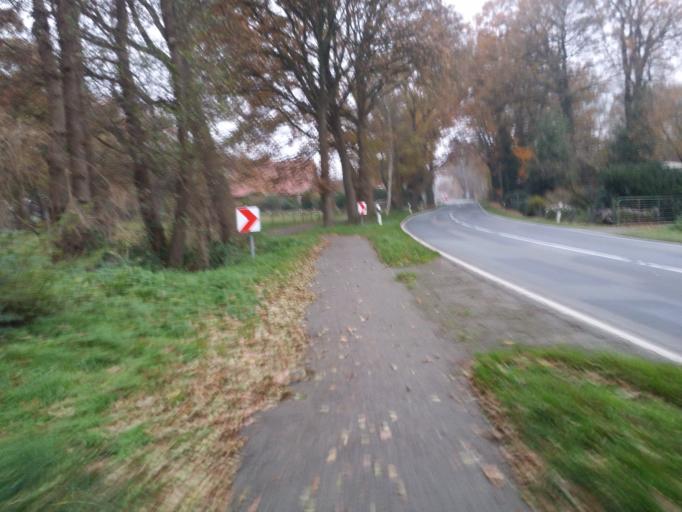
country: DE
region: Lower Saxony
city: Gross Ippener
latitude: 53.0145
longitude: 8.5881
